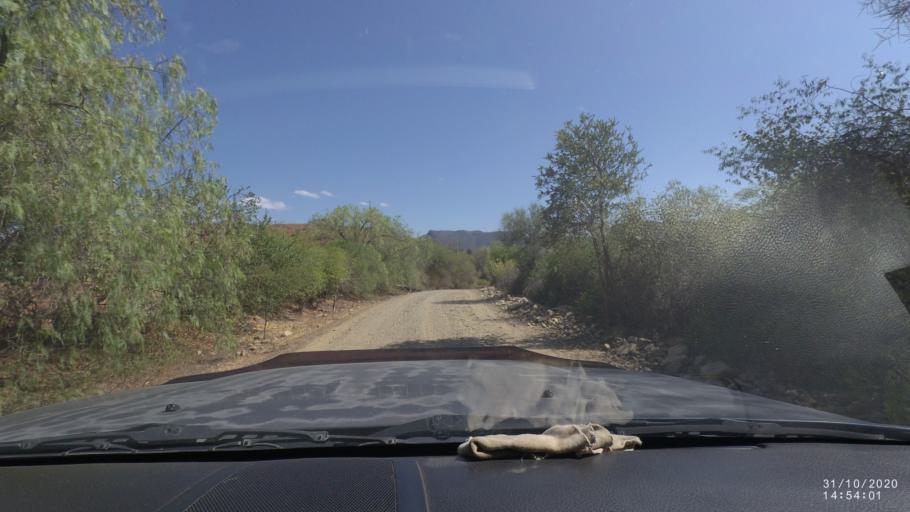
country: BO
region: Cochabamba
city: Aiquile
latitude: -18.2232
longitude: -64.8571
